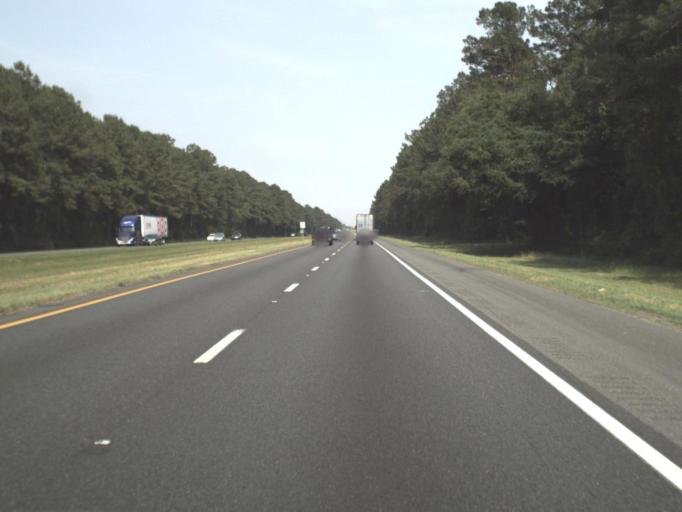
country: US
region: Florida
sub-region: Baker County
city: Macclenny
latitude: 30.2607
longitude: -82.1508
